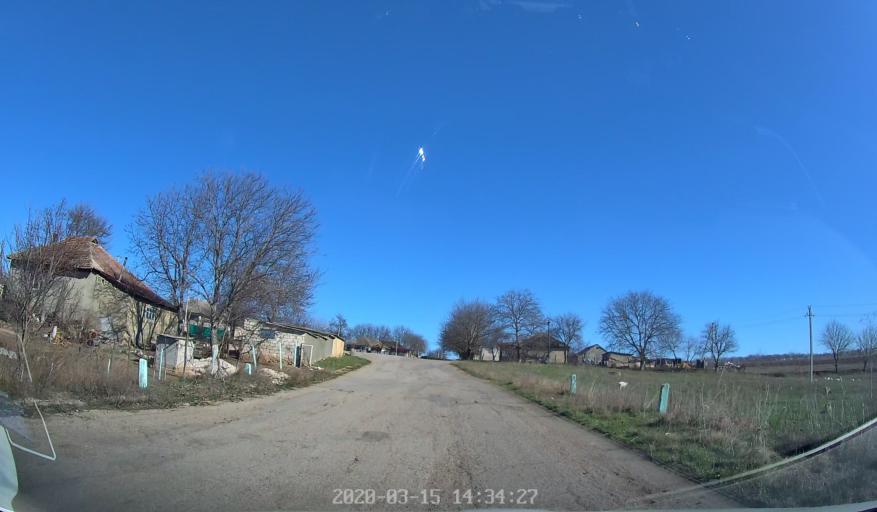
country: MD
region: Orhei
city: Orhei
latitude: 47.3321
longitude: 28.9194
